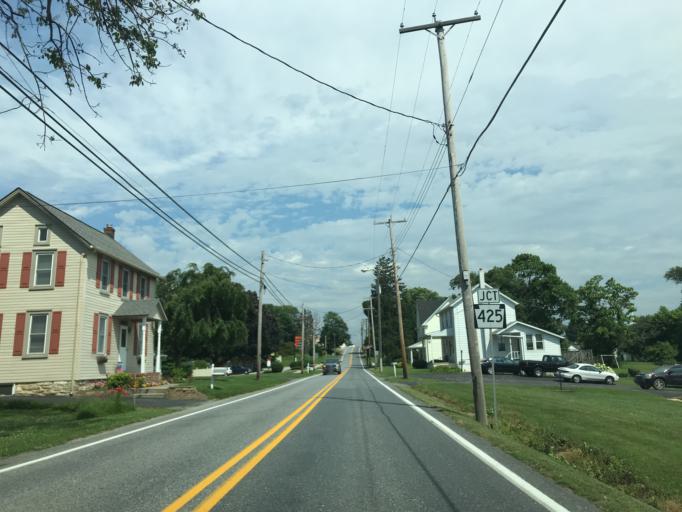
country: US
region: Pennsylvania
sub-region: York County
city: Susquehanna Trails
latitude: 39.7287
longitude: -76.4556
